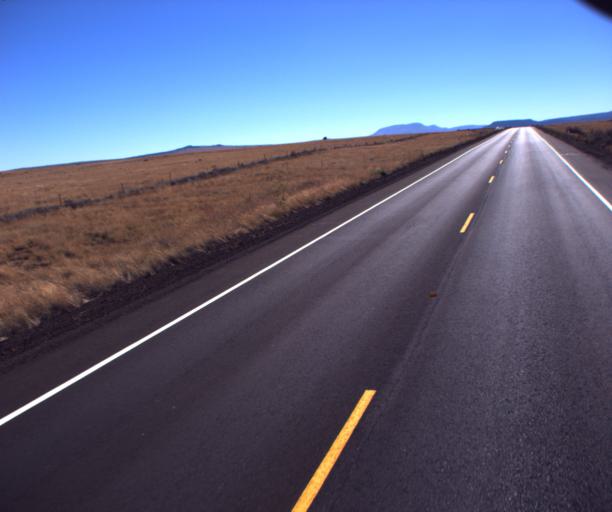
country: US
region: Arizona
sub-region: Apache County
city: Springerville
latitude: 34.2372
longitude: -109.3442
